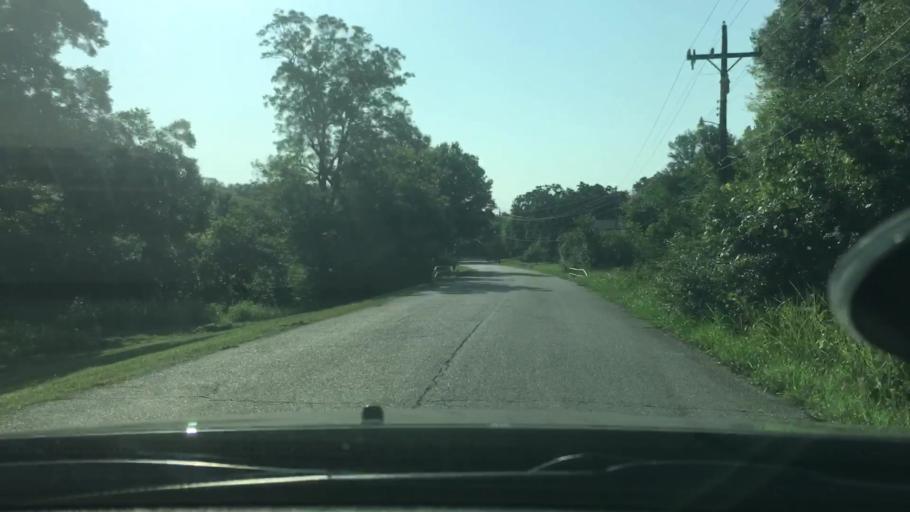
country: US
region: Oklahoma
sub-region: Atoka County
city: Atoka
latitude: 34.3902
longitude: -96.1324
